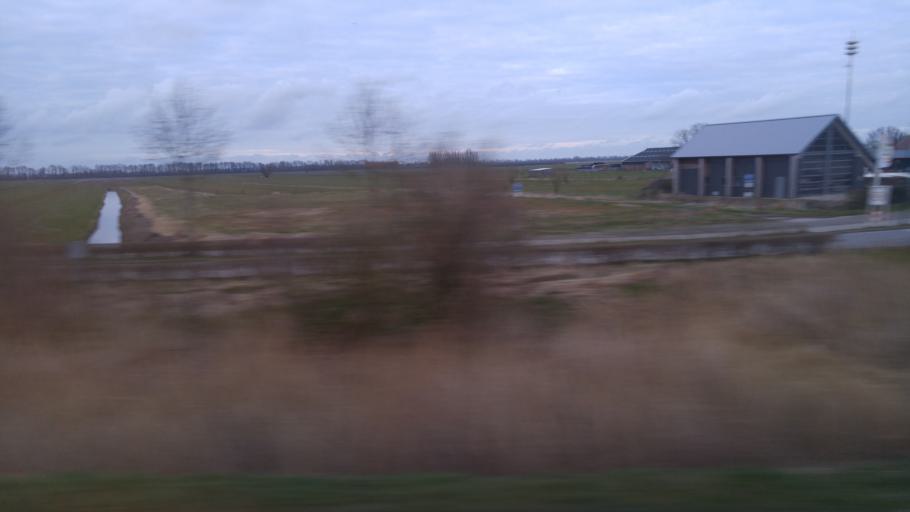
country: NL
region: Utrecht
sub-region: Gemeente Houten
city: Houten
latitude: 51.9927
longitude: 5.1913
